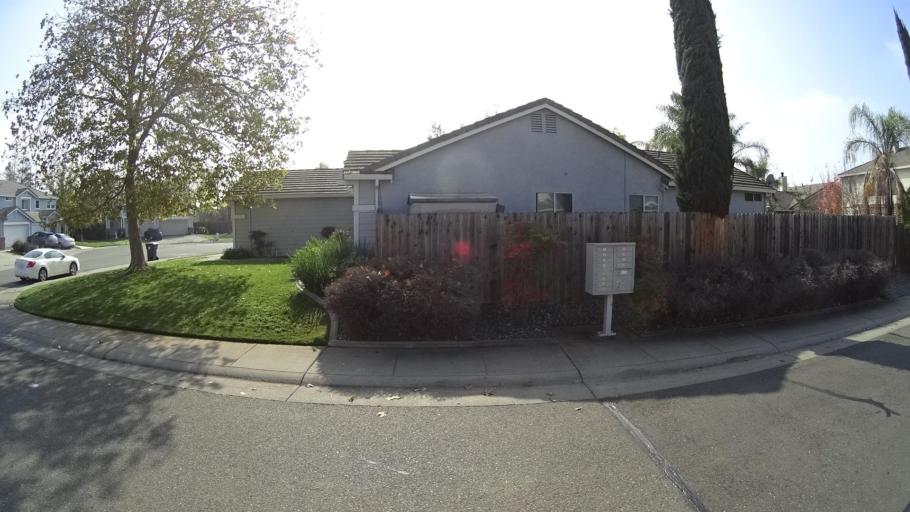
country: US
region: California
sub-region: Sacramento County
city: Vineyard
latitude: 38.4425
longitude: -121.3663
